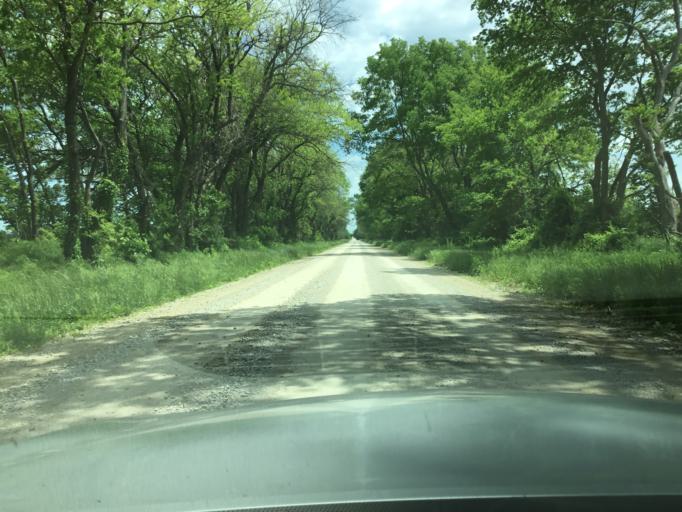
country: US
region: Kansas
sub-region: Montgomery County
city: Independence
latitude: 37.1095
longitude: -95.7731
